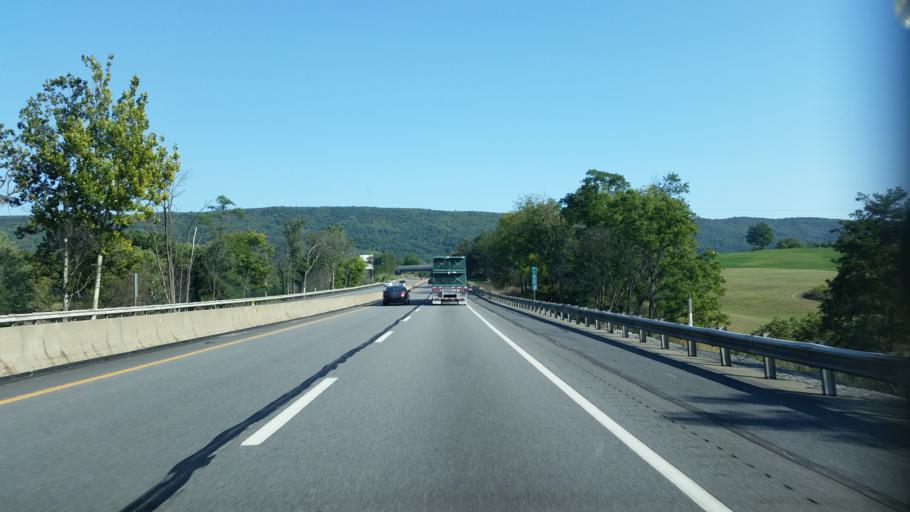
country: US
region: Pennsylvania
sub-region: Bedford County
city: Bedford
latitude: 40.0086
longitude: -78.4390
